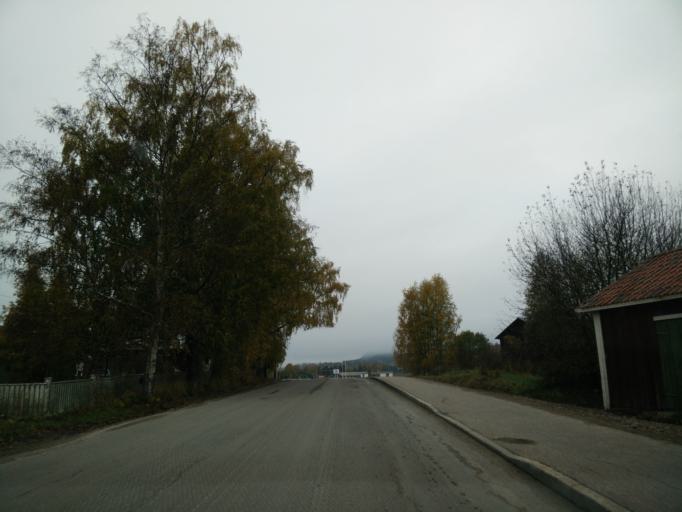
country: SE
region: Vaesternorrland
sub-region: Sundsvalls Kommun
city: Nolby
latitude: 62.2926
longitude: 17.3581
